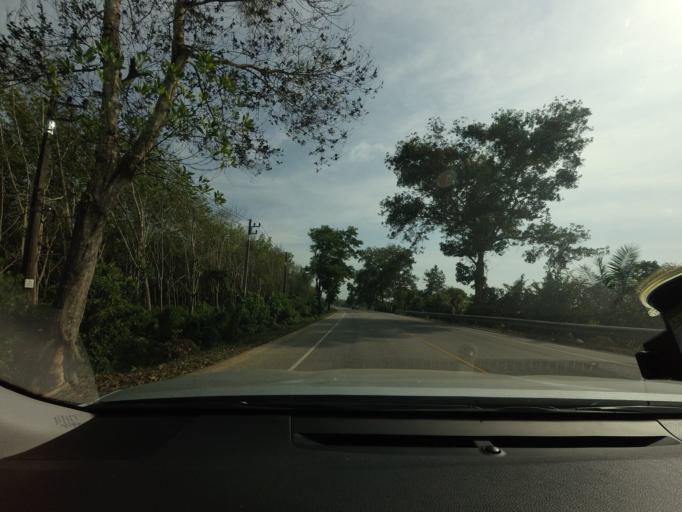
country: TH
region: Narathiwat
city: Ra-ngae
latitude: 6.3401
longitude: 101.7901
